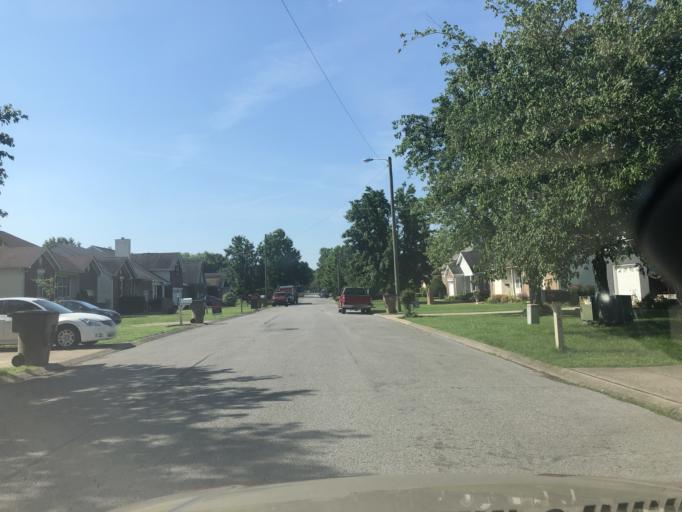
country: US
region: Tennessee
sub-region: Davidson County
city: Lakewood
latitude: 36.2384
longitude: -86.6997
